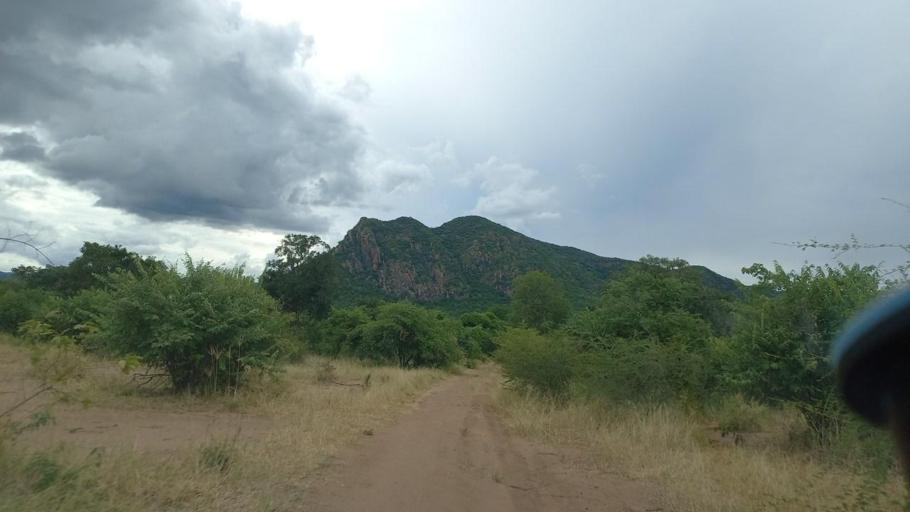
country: ZM
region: Lusaka
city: Luangwa
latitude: -15.6183
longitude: 30.2688
